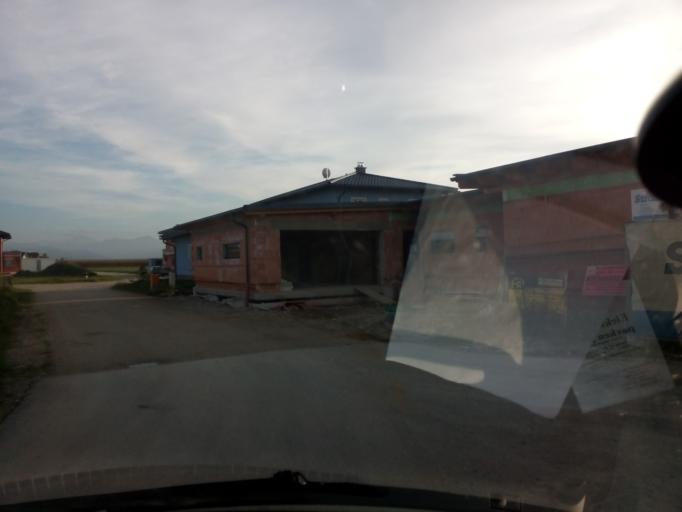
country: AT
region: Upper Austria
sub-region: Politischer Bezirk Gmunden
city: Vorchdorf
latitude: 48.0437
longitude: 13.9747
